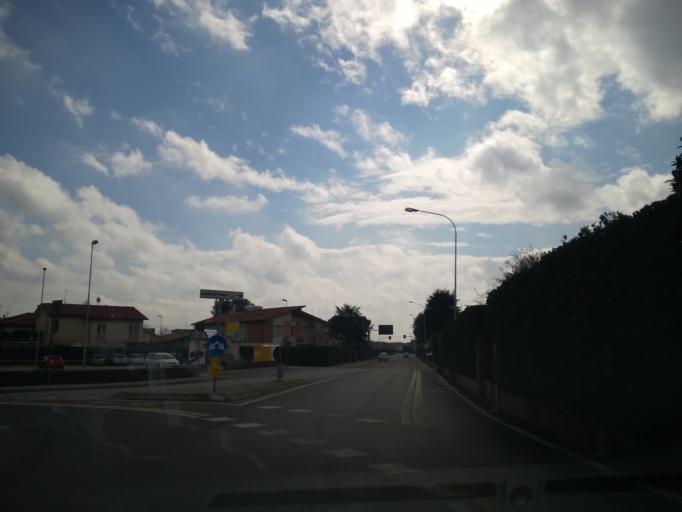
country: IT
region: Veneto
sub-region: Provincia di Vicenza
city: Thiene
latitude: 45.7113
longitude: 11.4671
